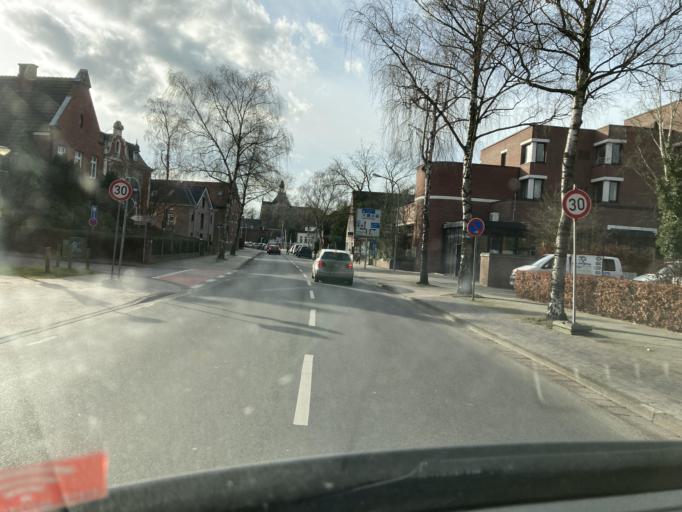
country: DE
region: Lower Saxony
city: Leer
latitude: 53.2333
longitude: 7.4548
